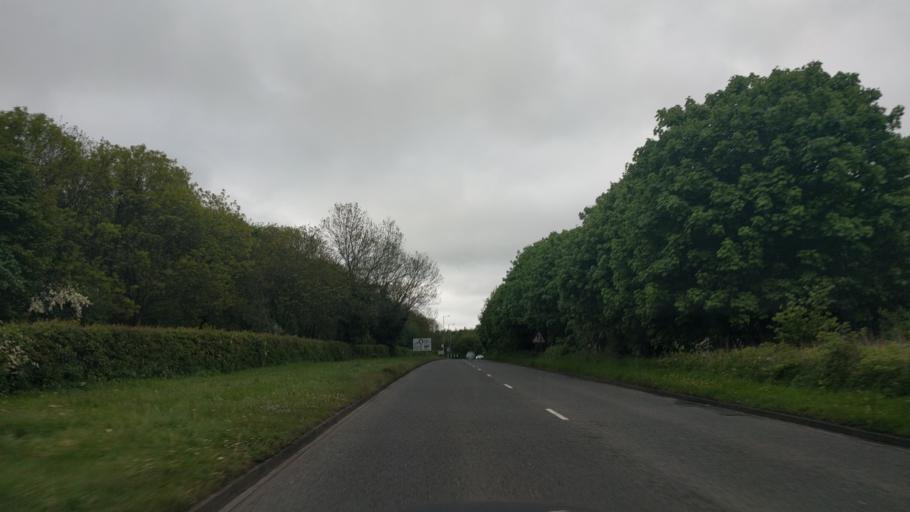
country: GB
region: England
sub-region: Northumberland
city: Cramlington
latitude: 55.0997
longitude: -1.5954
